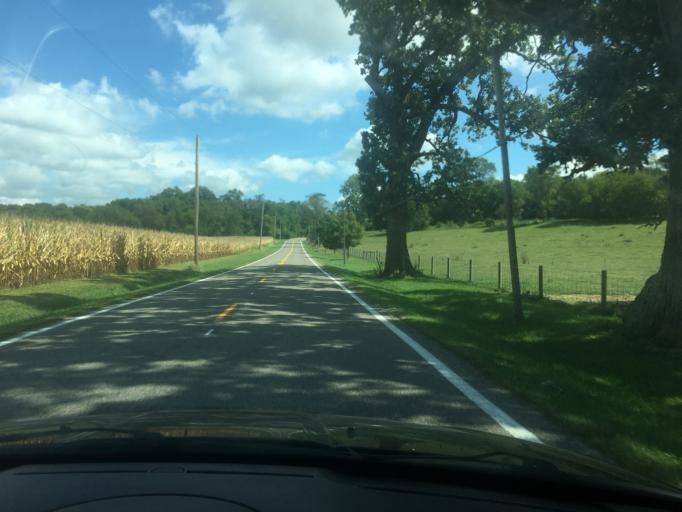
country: US
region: Ohio
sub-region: Logan County
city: West Liberty
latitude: 40.2346
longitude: -83.7264
